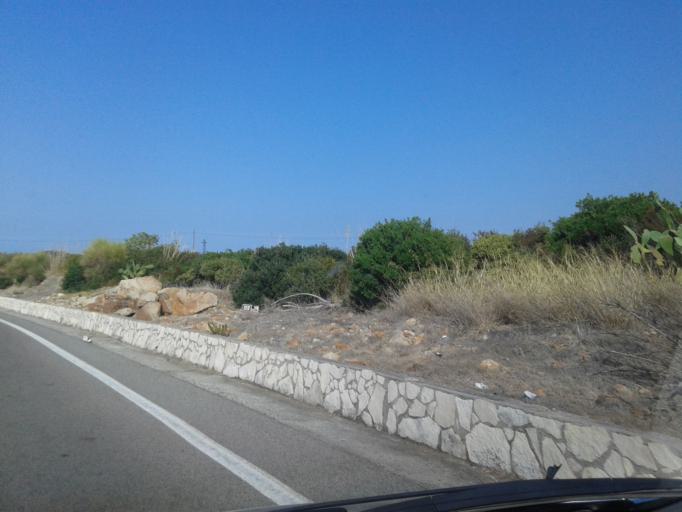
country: IT
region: Sicily
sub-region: Palermo
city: Finale
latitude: 38.0236
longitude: 14.1453
